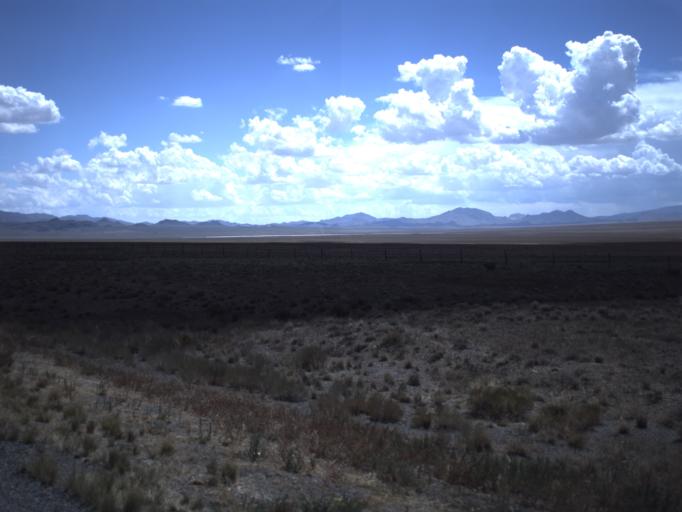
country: US
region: Nevada
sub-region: White Pine County
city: McGill
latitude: 39.0404
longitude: -113.8310
